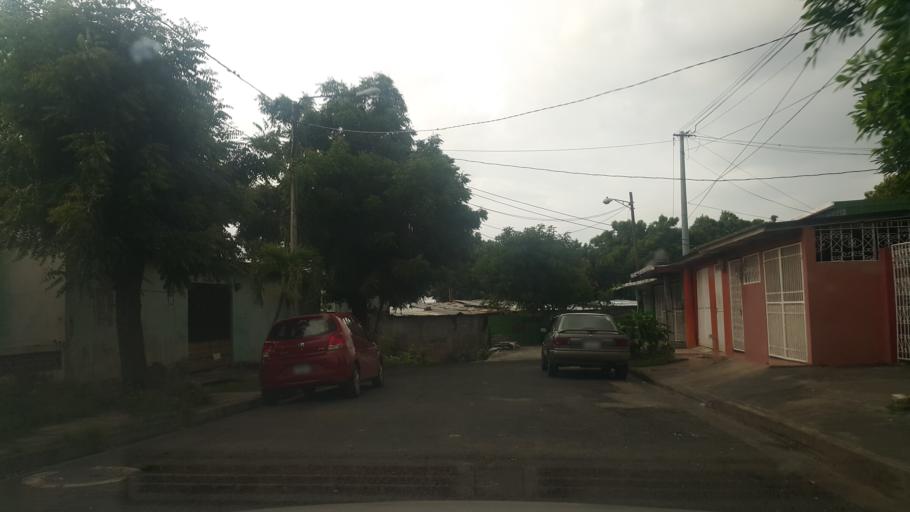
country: NI
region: Managua
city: Managua
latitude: 12.1318
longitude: -86.2985
